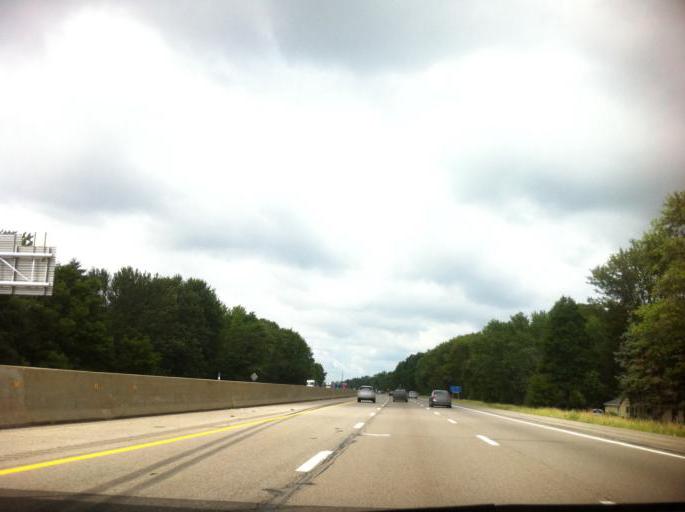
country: US
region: Ohio
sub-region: Lorain County
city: North Ridgeville
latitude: 41.3799
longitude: -82.0163
